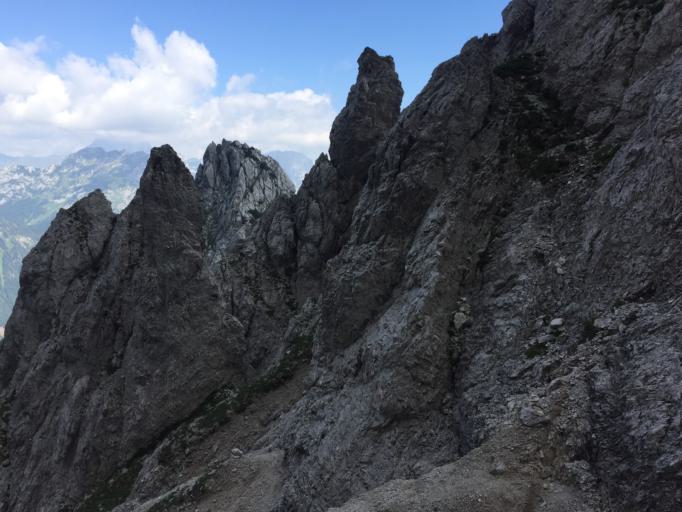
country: IT
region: Friuli Venezia Giulia
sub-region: Provincia di Udine
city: Forni Avoltri
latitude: 46.5526
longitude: 12.7689
